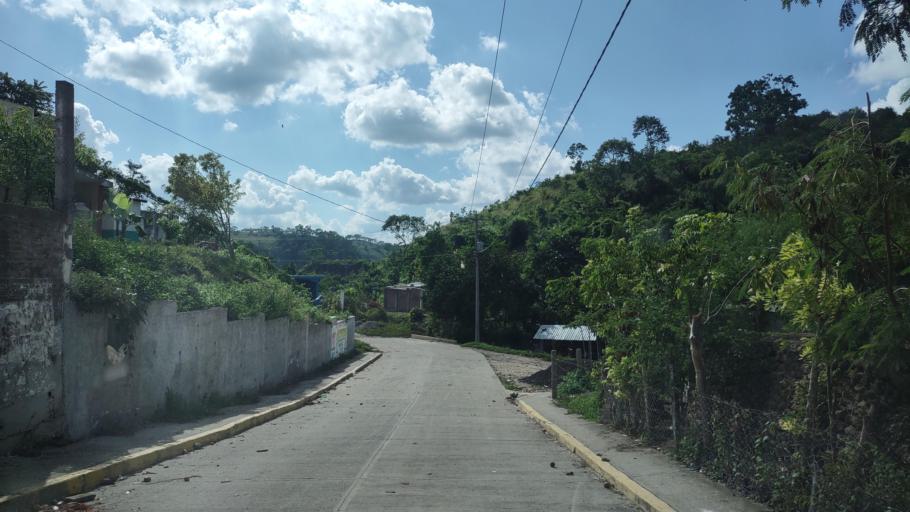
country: MM
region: Shan
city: Taunggyi
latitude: 20.5533
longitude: 97.3412
